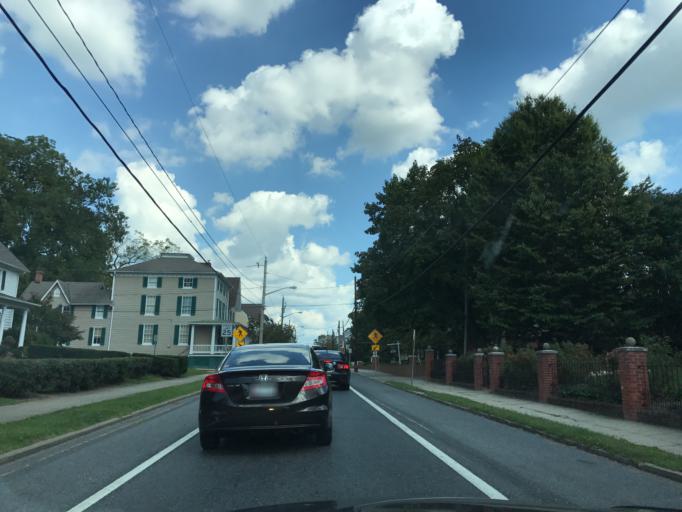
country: US
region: Maryland
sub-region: Queen Anne's County
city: Centreville
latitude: 39.0428
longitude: -76.0665
